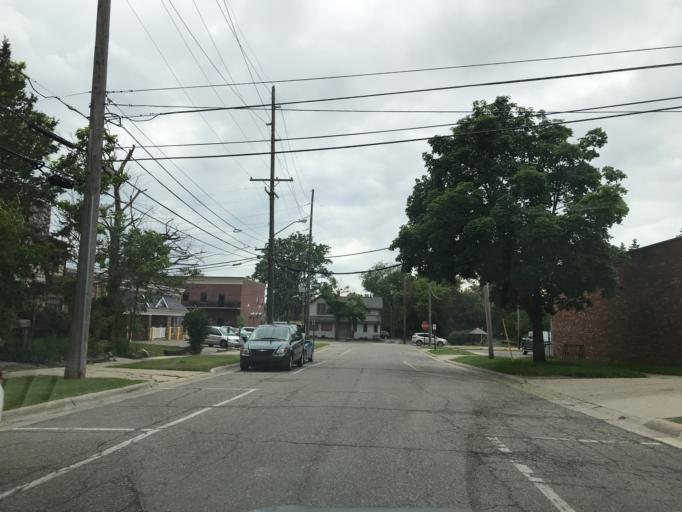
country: US
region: Michigan
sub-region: Oakland County
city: South Lyon
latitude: 42.4621
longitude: -83.6505
